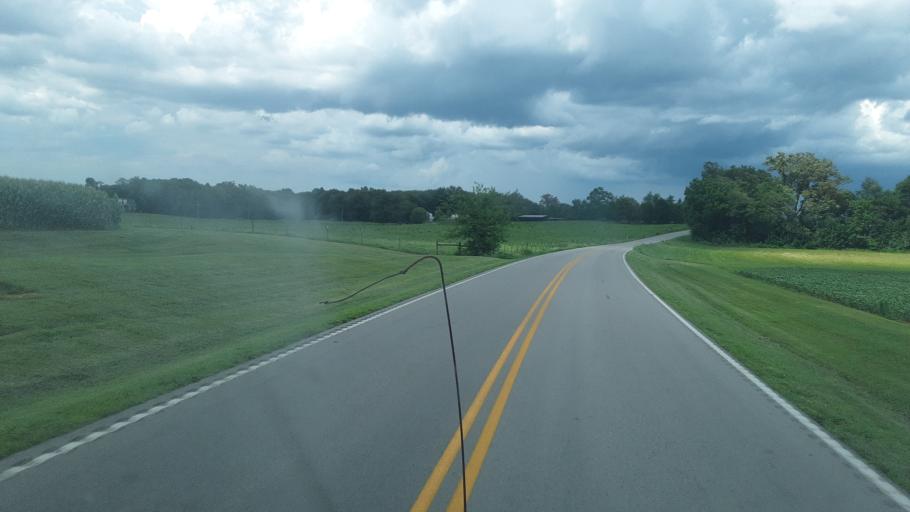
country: US
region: Kentucky
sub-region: Todd County
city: Elkton
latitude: 36.7339
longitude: -87.1880
